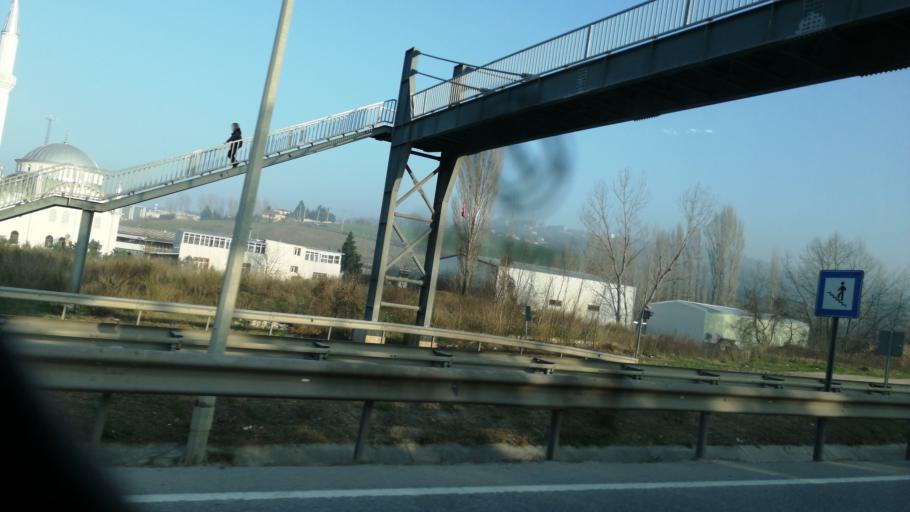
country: TR
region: Yalova
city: Yalova
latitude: 40.6231
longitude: 29.2707
